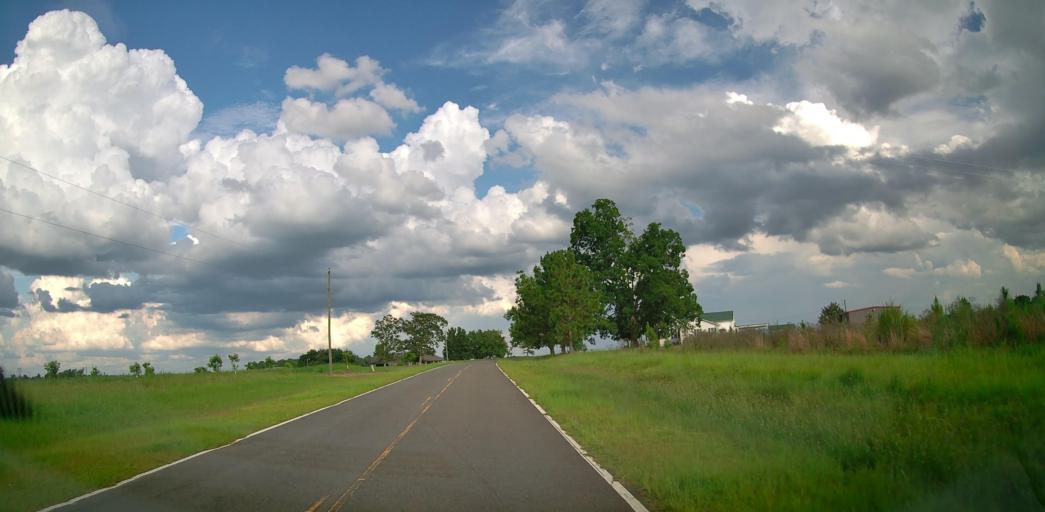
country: US
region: Georgia
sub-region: Bleckley County
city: Cochran
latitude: 32.4091
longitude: -83.4283
